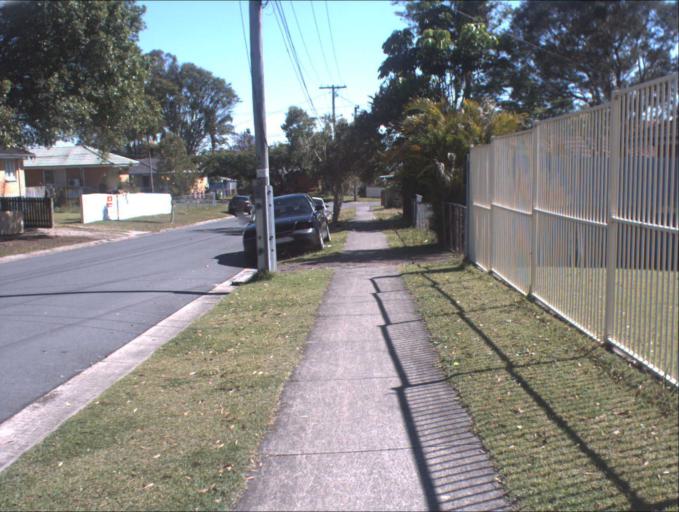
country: AU
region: Queensland
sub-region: Logan
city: Logan City
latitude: -27.6268
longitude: 153.1108
